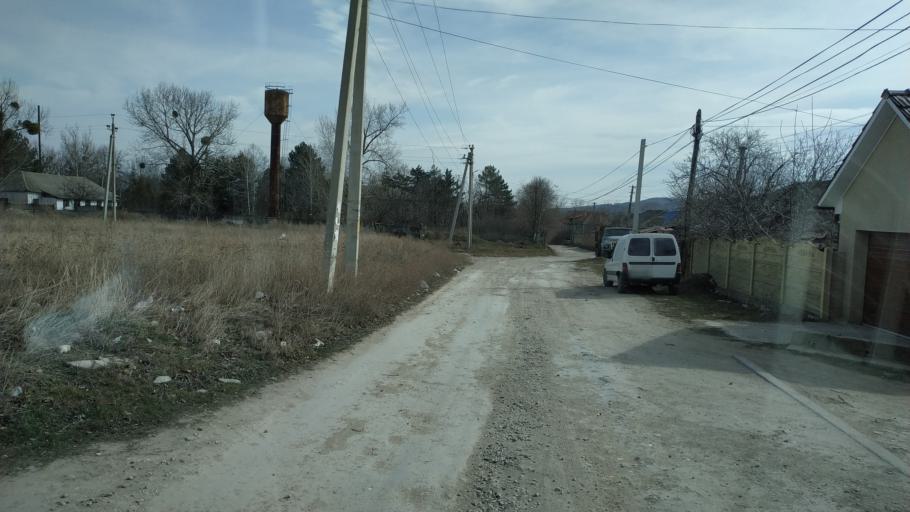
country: MD
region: Chisinau
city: Vatra
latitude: 47.0963
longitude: 28.6745
